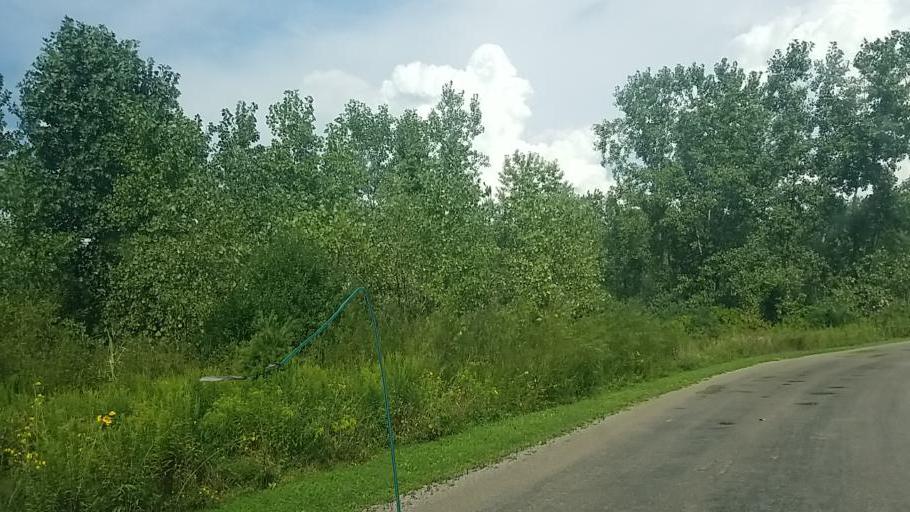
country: US
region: Ohio
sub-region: Medina County
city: Lodi
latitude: 41.0048
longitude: -81.9774
